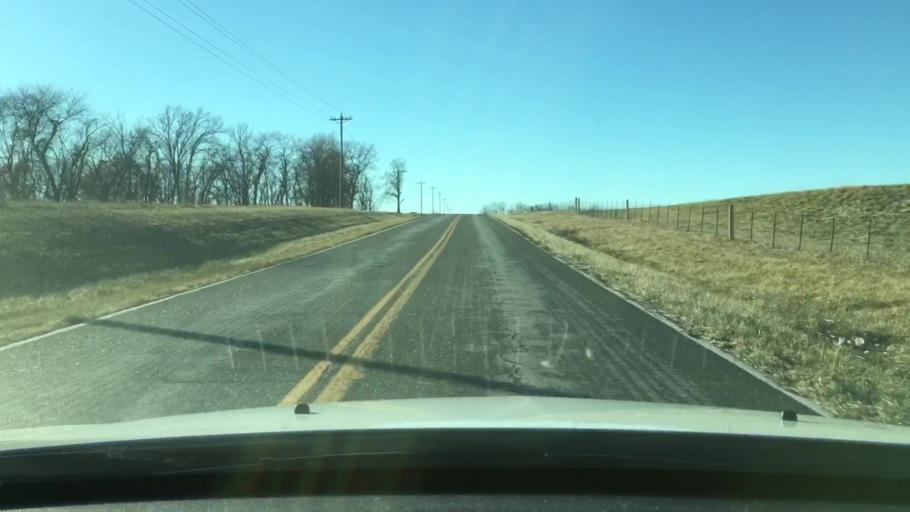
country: US
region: Missouri
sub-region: Audrain County
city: Mexico
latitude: 39.2766
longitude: -91.7827
